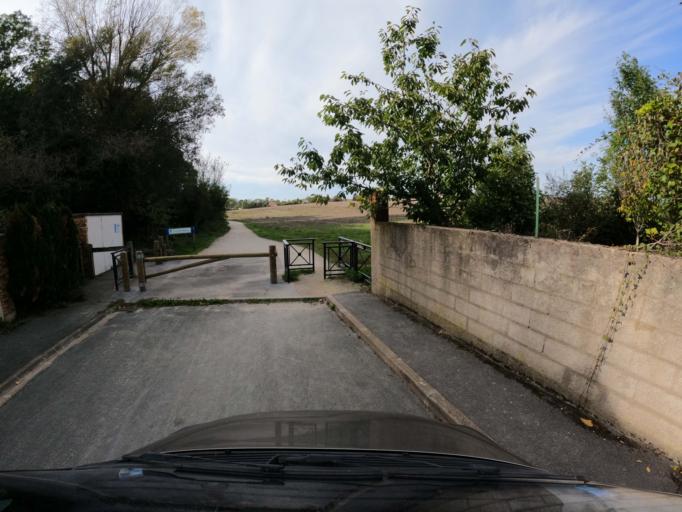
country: FR
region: Ile-de-France
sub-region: Departement du Val-de-Marne
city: La Queue-en-Brie
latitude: 48.7838
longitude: 2.5917
